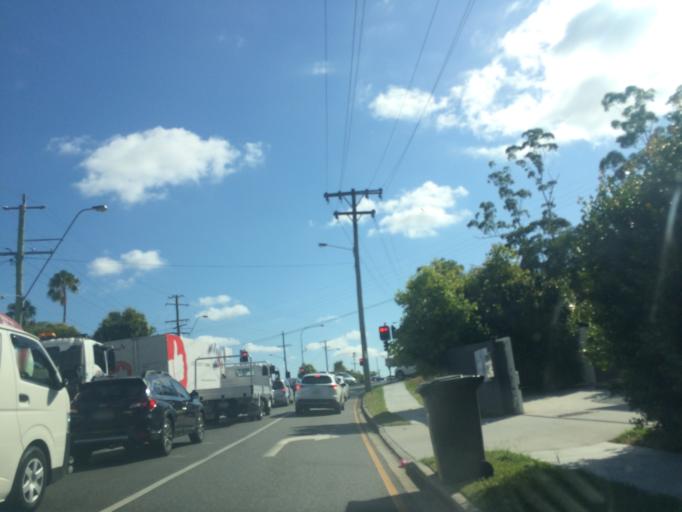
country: AU
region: Queensland
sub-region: Brisbane
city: Morningside
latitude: -27.4707
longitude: 153.0628
